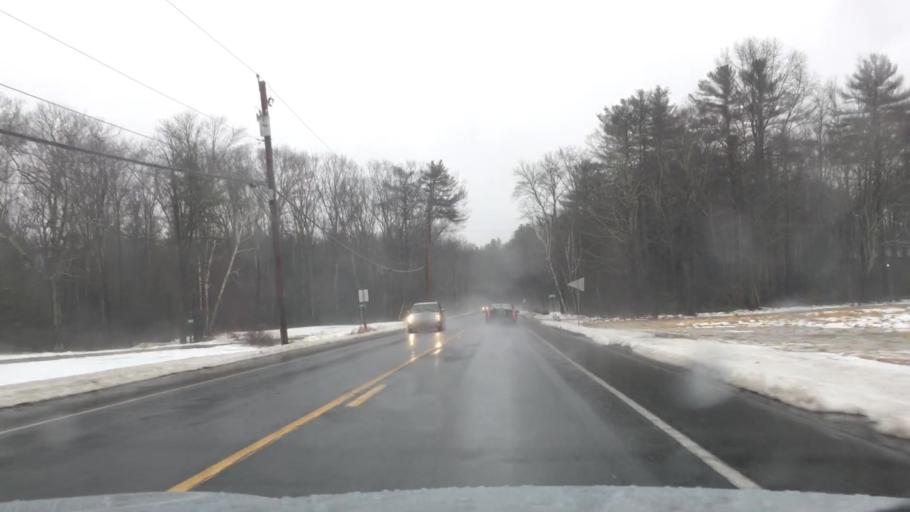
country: US
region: Massachusetts
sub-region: Franklin County
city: Orange
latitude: 42.5432
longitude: -72.3002
